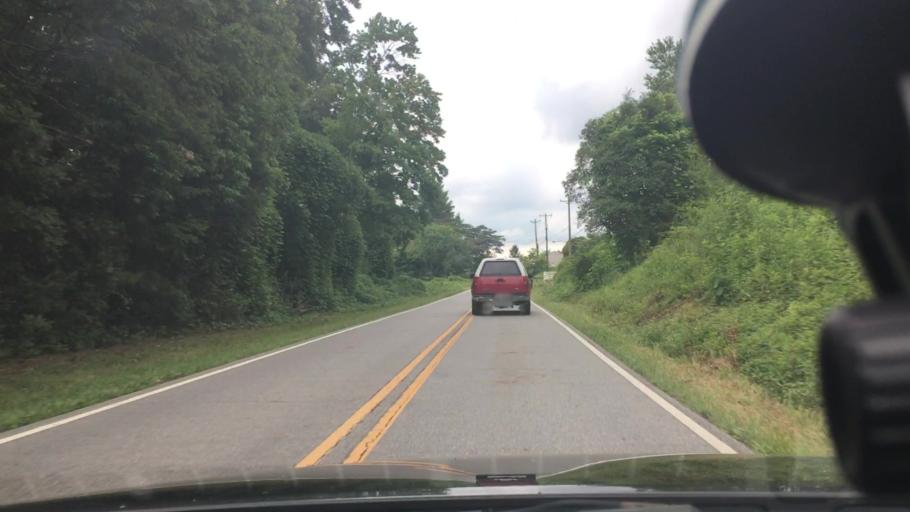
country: US
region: North Carolina
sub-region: McDowell County
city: West Marion
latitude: 35.6521
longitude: -82.0148
